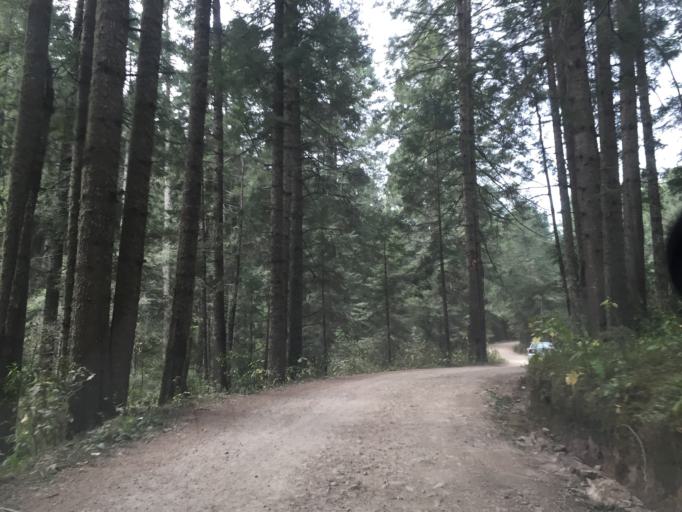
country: MX
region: Michoacan
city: Mineral de Angangueo
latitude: 19.6677
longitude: -100.2760
